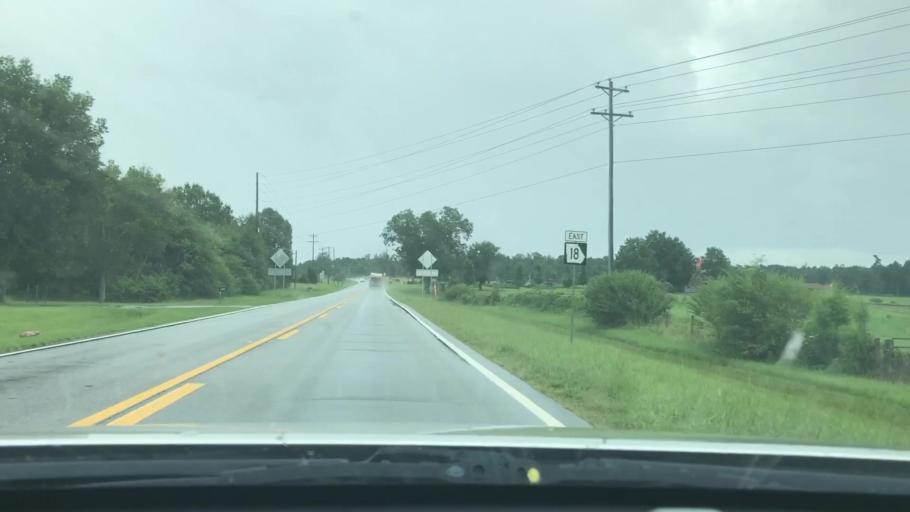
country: US
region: Georgia
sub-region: Lamar County
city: Barnesville
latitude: 33.0608
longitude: -84.2072
